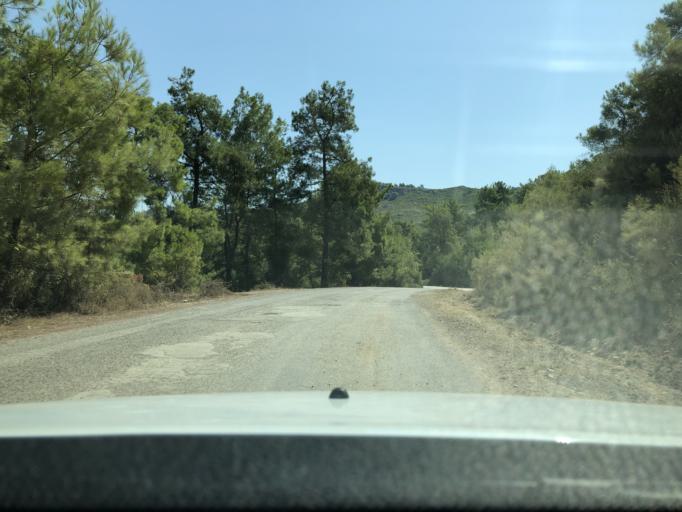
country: TR
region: Antalya
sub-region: Manavgat
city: Manavgat
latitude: 36.8260
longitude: 31.5112
